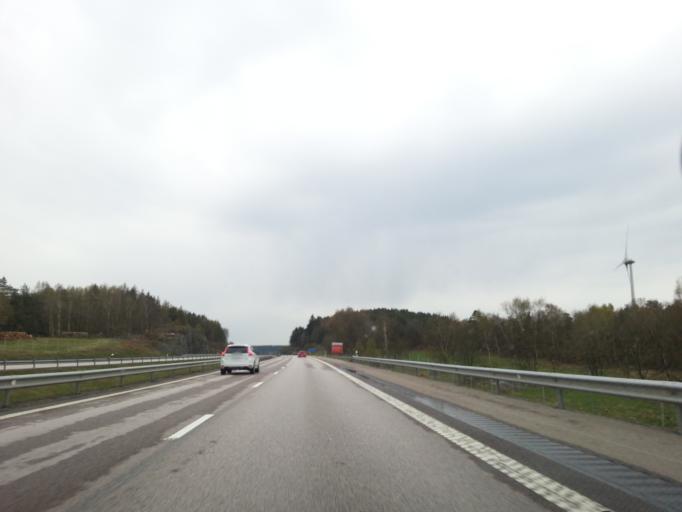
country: SE
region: Halland
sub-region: Kungsbacka Kommun
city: Frillesas
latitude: 57.3386
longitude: 12.2062
